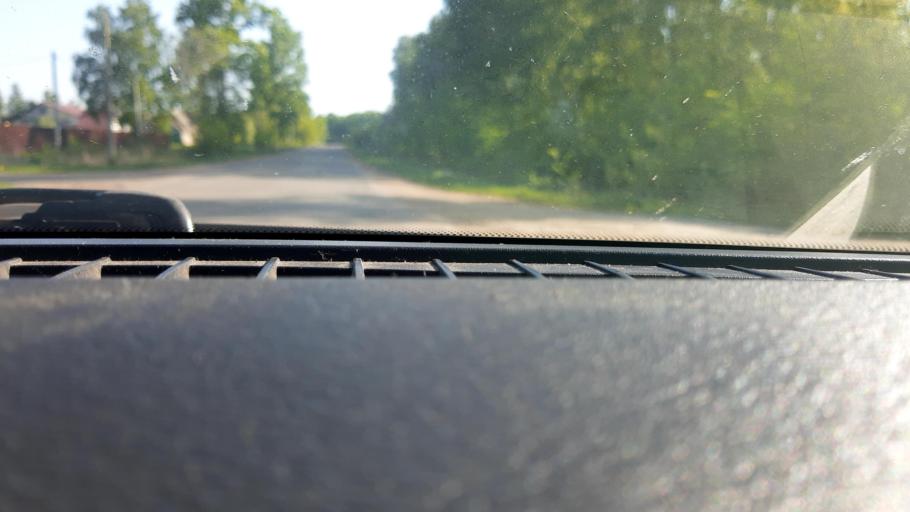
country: RU
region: Bashkortostan
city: Kabakovo
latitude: 54.7128
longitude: 56.2496
